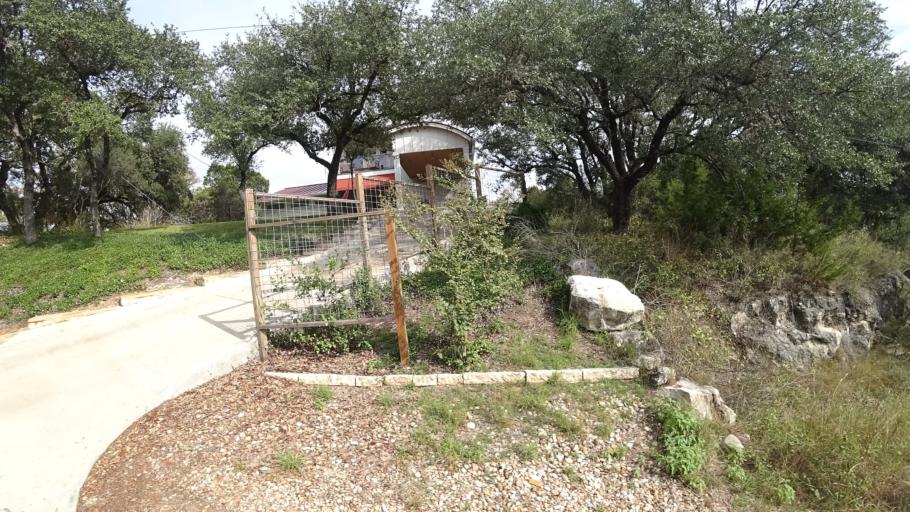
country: US
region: Texas
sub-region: Travis County
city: Hudson Bend
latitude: 30.3792
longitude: -97.9164
